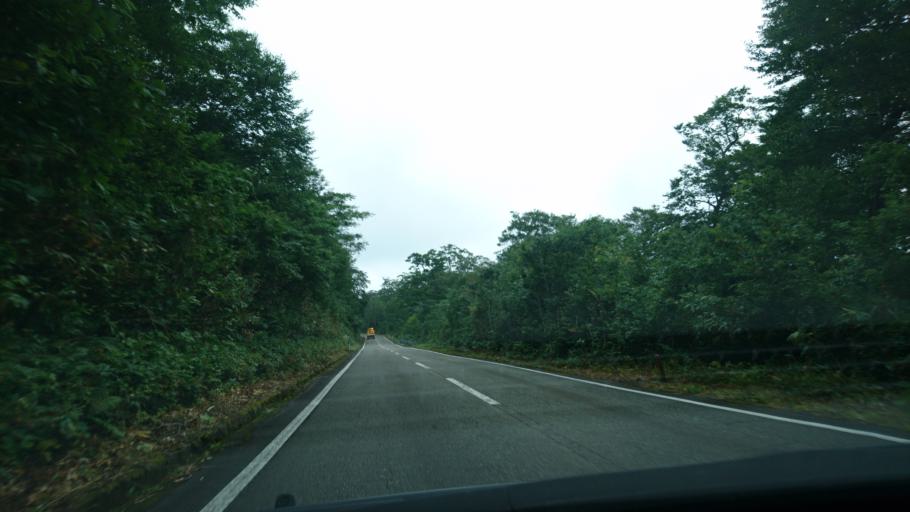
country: JP
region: Akita
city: Yuzawa
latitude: 38.9817
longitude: 140.7433
